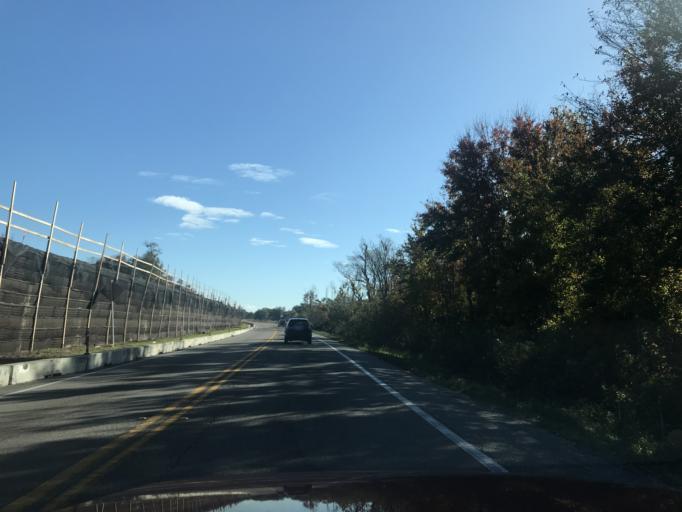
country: US
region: Florida
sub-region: Osceola County
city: Campbell
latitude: 28.2548
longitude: -81.4800
